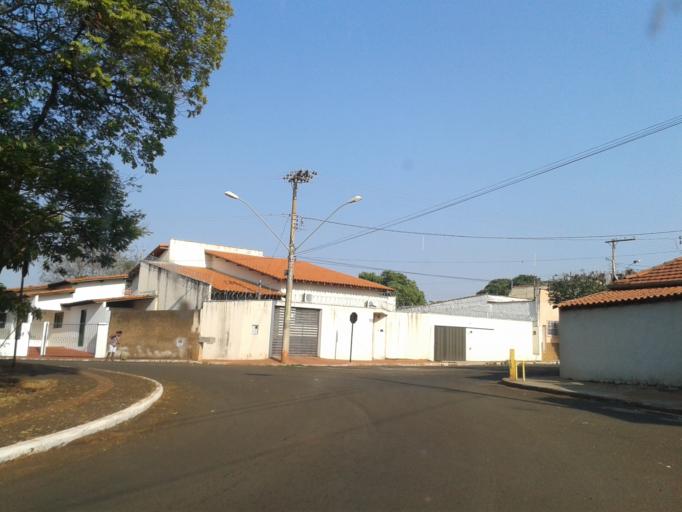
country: BR
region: Minas Gerais
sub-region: Ituiutaba
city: Ituiutaba
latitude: -18.9741
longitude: -49.4724
